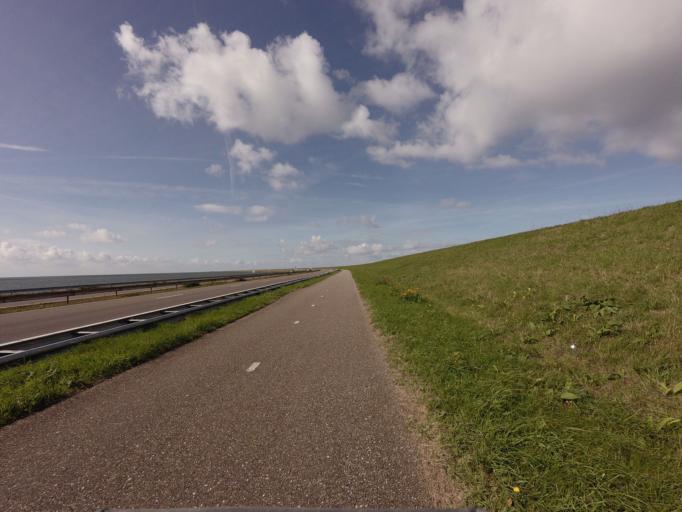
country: NL
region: Friesland
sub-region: Sudwest Fryslan
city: Makkum
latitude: 53.0694
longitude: 5.3044
